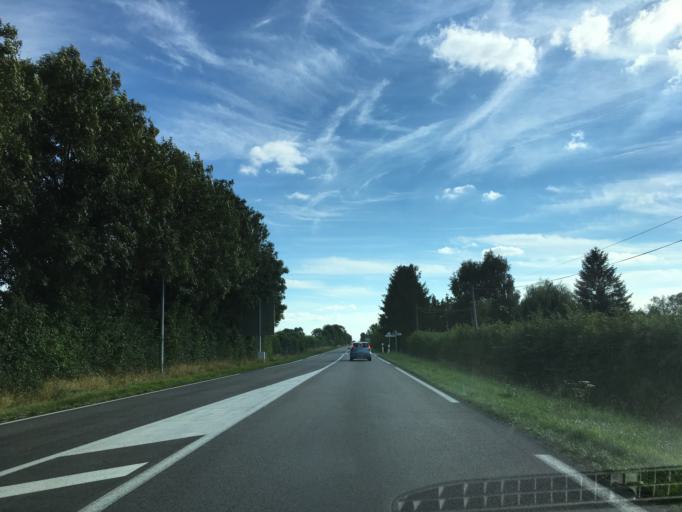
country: FR
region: Lower Normandy
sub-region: Departement du Calvados
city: Orbec
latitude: 48.9547
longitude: 0.4651
